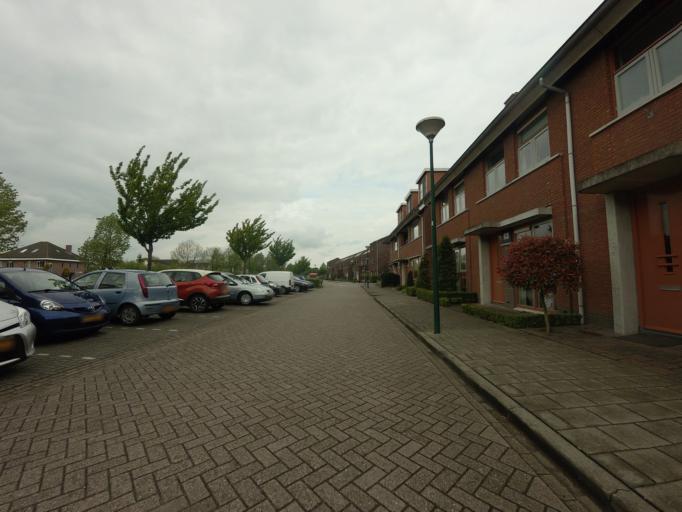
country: NL
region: Utrecht
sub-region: Gemeente Montfoort
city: Montfoort
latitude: 52.0404
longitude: 4.9573
